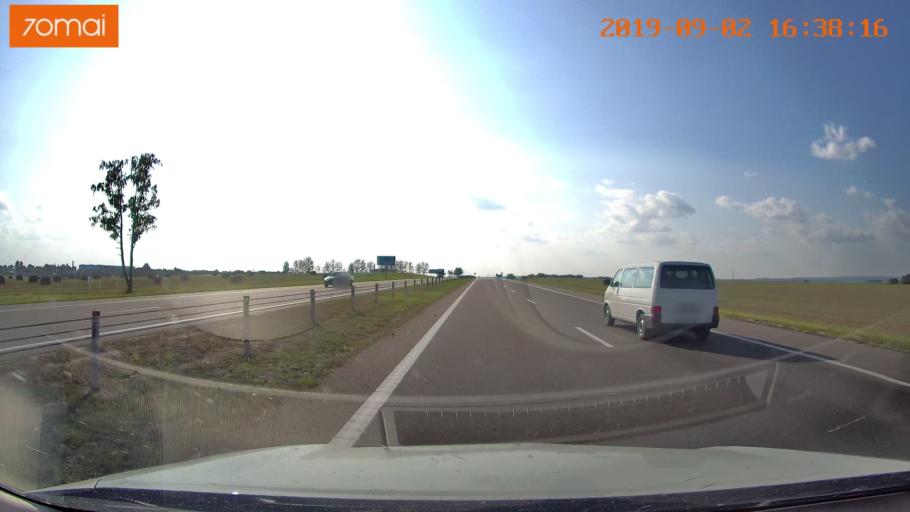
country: BY
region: Minsk
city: Zamostochcha
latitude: 53.7615
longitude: 27.9216
